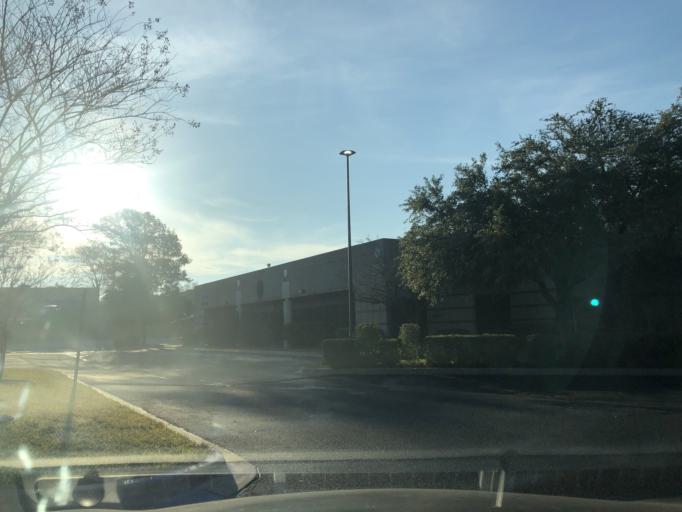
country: US
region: Texas
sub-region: Travis County
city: Wells Branch
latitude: 30.4352
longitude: -97.6845
